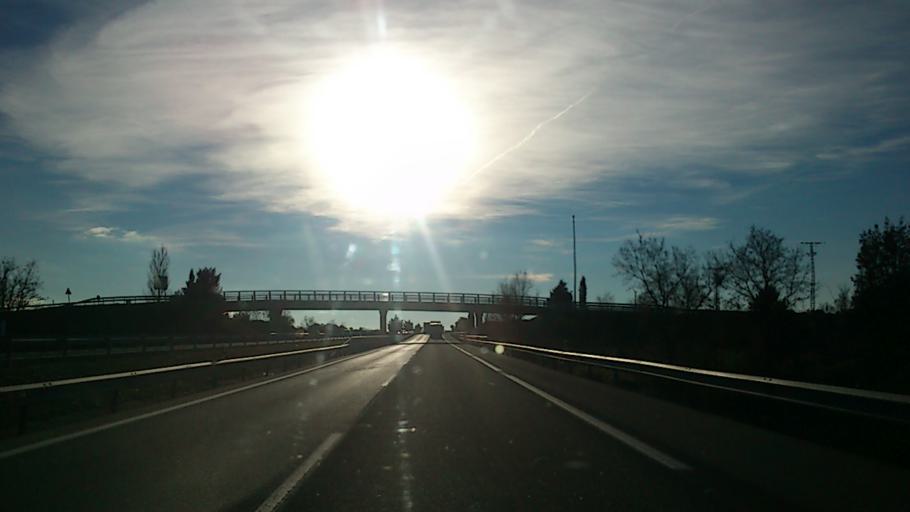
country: ES
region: Castille-La Mancha
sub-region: Provincia de Guadalajara
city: Mirabueno
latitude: 40.9133
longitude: -2.7372
